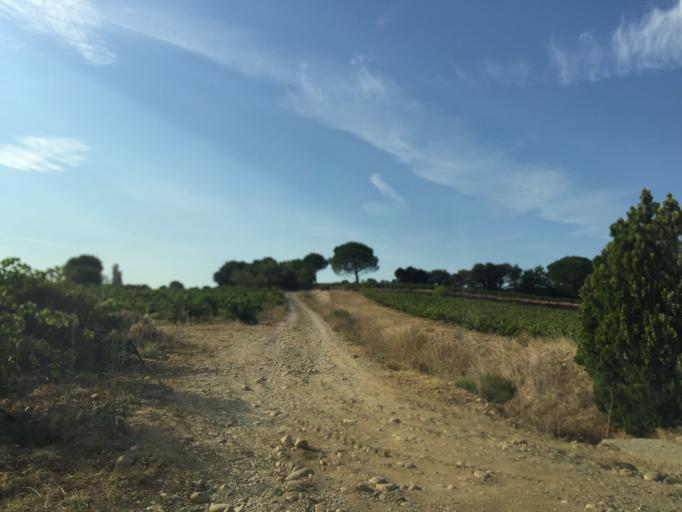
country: FR
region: Provence-Alpes-Cote d'Azur
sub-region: Departement du Vaucluse
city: Chateauneuf-du-Pape
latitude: 44.0761
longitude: 4.8548
